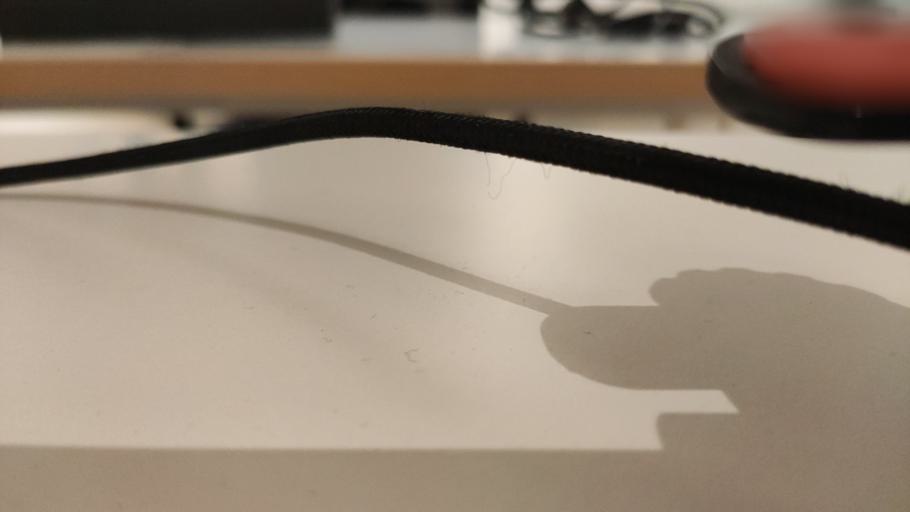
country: RU
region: Moskovskaya
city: Dorokhovo
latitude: 55.4929
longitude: 36.3519
